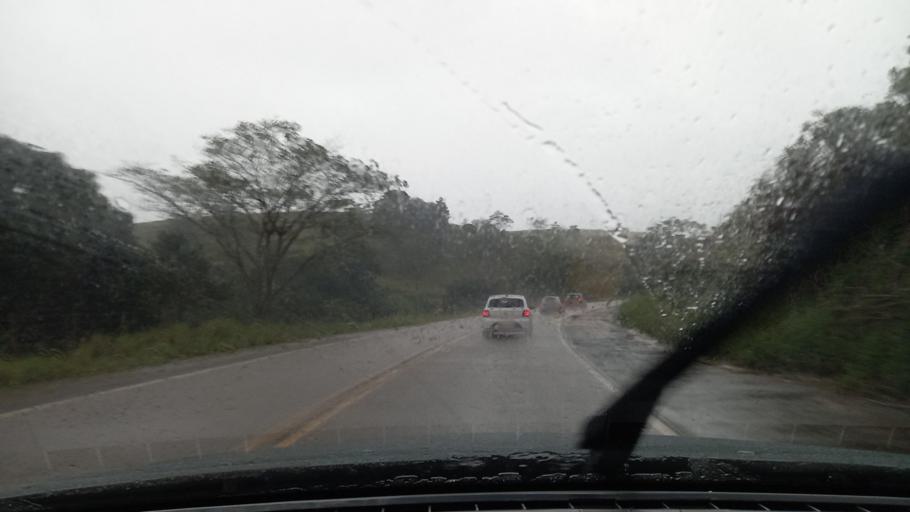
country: BR
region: Pernambuco
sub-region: Rio Formoso
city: Rio Formoso
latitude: -8.6993
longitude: -35.1548
